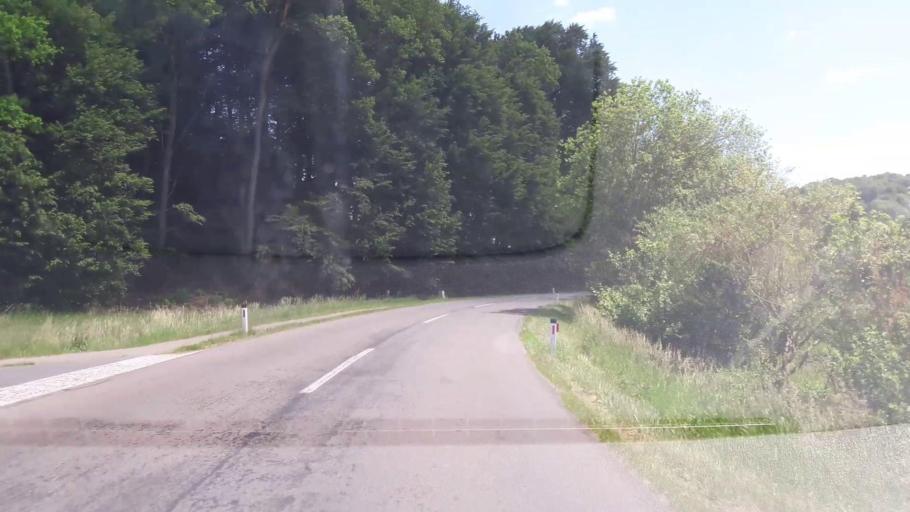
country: AT
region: Styria
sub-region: Politischer Bezirk Suedoststeiermark
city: Unterlamm
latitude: 46.9710
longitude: 16.0698
